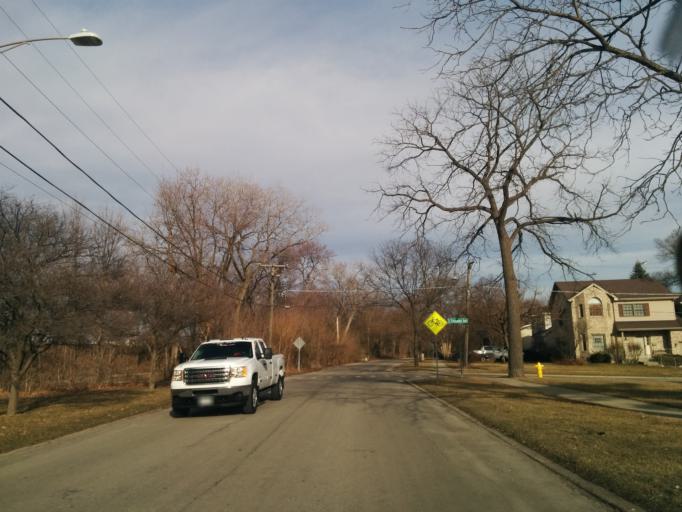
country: US
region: Illinois
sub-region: DuPage County
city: Lombard
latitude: 41.8897
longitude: -88.0042
